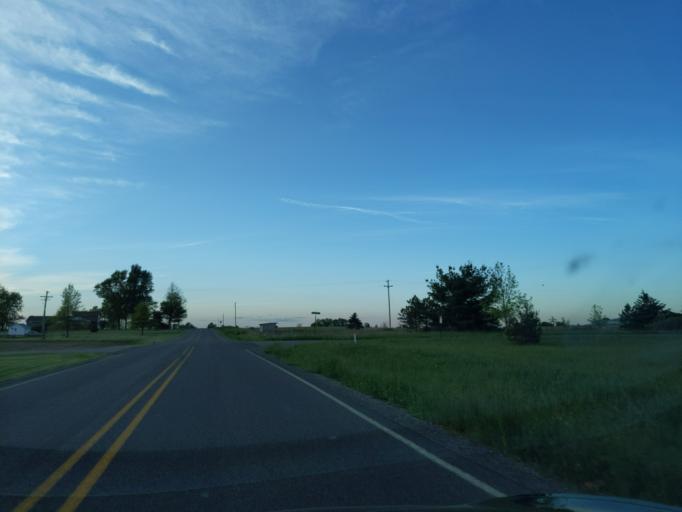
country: US
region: Michigan
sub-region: Ingham County
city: Williamston
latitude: 42.5842
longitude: -84.2986
